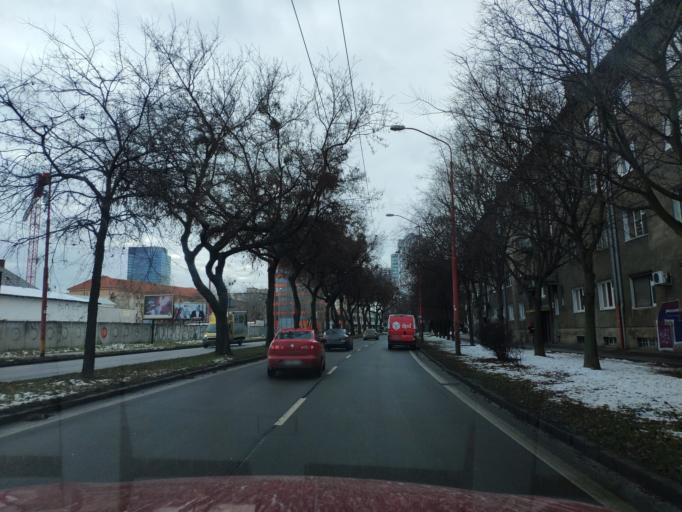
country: SK
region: Bratislavsky
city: Bratislava
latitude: 48.1527
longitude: 17.1257
